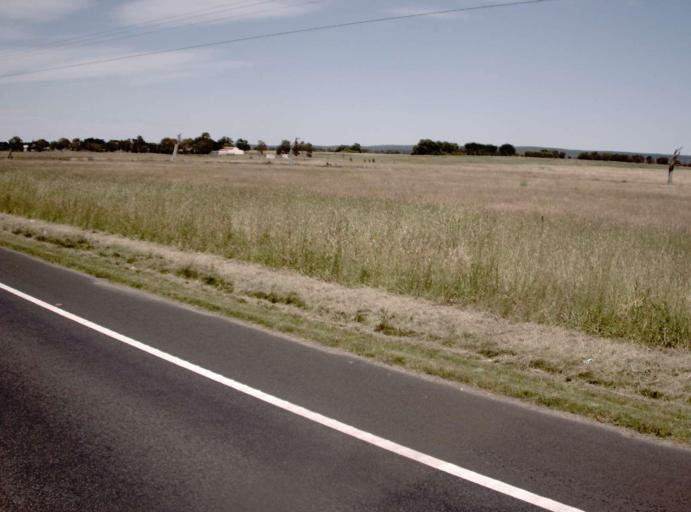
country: AU
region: Victoria
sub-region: Wellington
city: Heyfield
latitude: -38.1576
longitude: 146.7456
